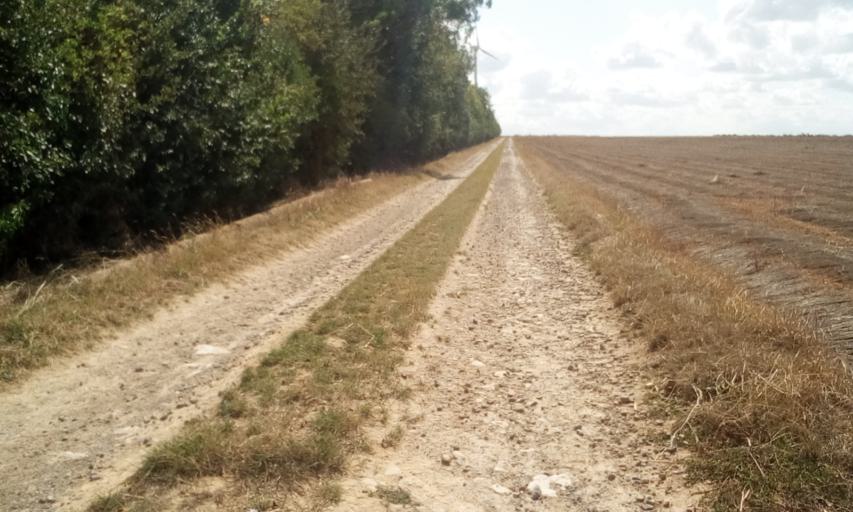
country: FR
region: Lower Normandy
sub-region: Departement du Calvados
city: Bellengreville
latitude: 49.1011
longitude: -0.2218
